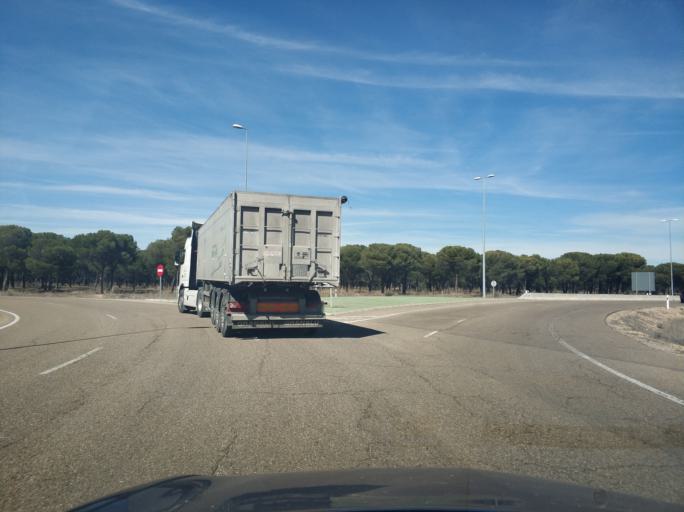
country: ES
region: Castille and Leon
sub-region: Provincia de Valladolid
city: Viana de Cega
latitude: 41.5622
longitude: -4.7862
